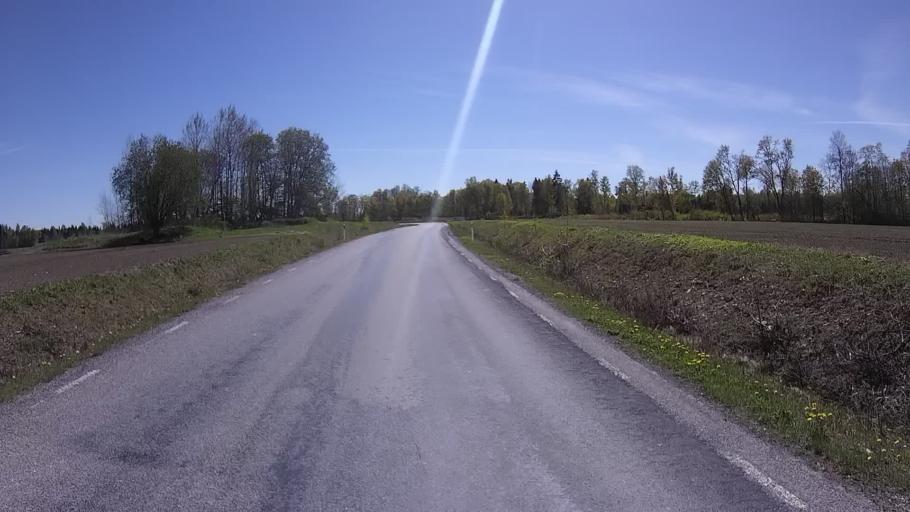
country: EE
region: Harju
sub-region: Raasiku vald
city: Raasiku
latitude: 59.0919
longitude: 25.1733
